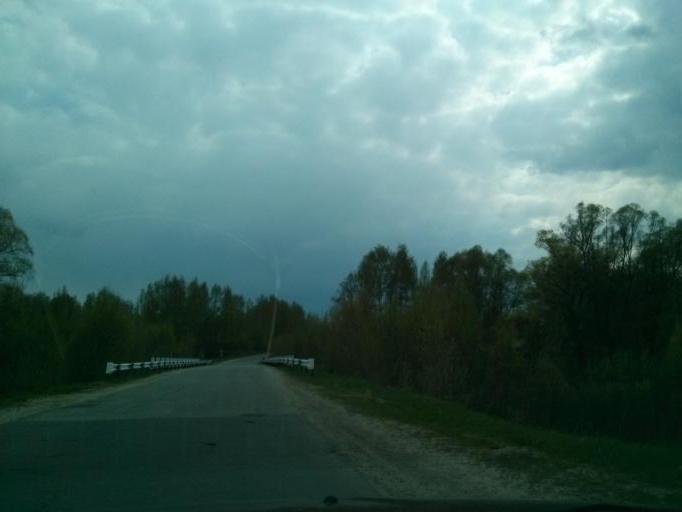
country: RU
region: Nizjnij Novgorod
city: Shimorskoye
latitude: 55.3473
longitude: 41.9305
